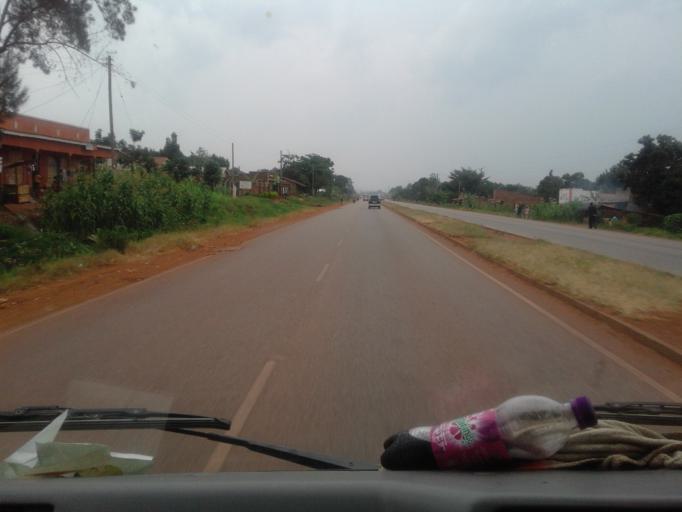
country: UG
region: Eastern Region
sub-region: Jinja District
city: Bugembe
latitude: 0.4710
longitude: 33.2509
